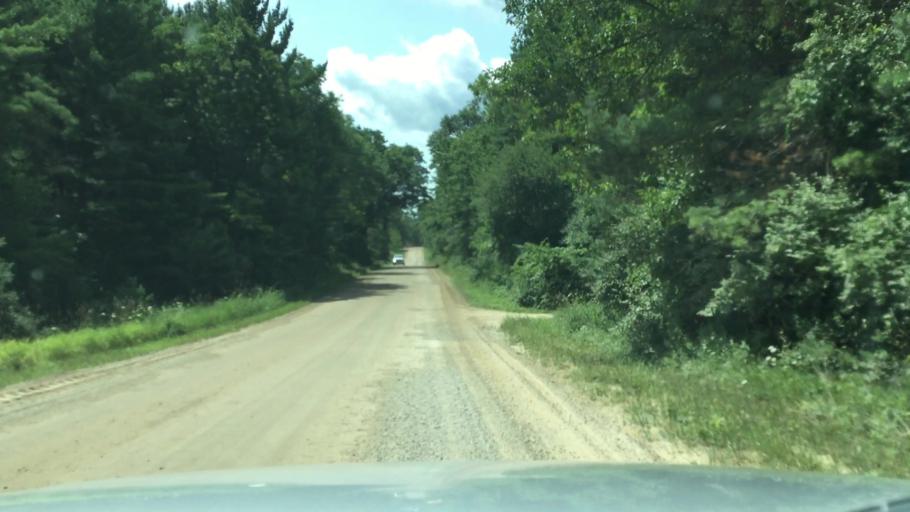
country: US
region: Michigan
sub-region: Ionia County
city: Belding
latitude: 43.1378
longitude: -85.2135
